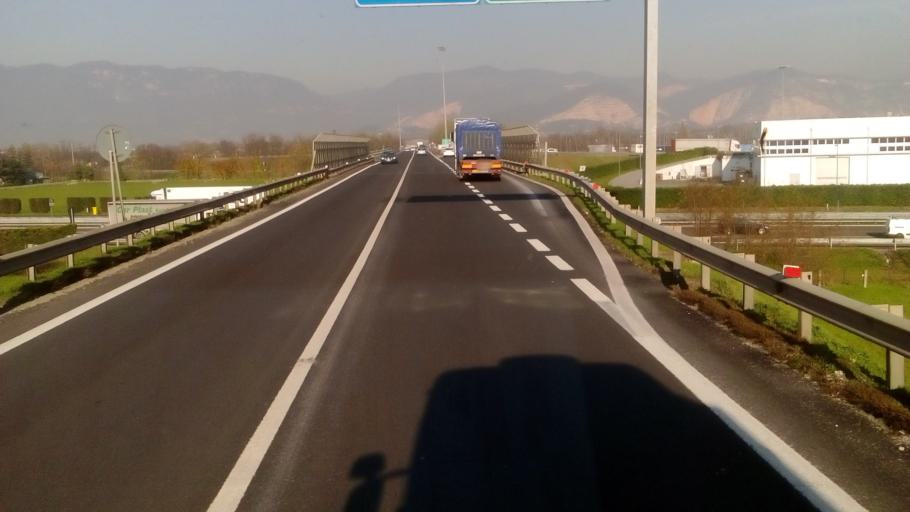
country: IT
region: Lombardy
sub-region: Provincia di Brescia
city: Castenedolo
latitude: 45.4823
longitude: 10.3186
